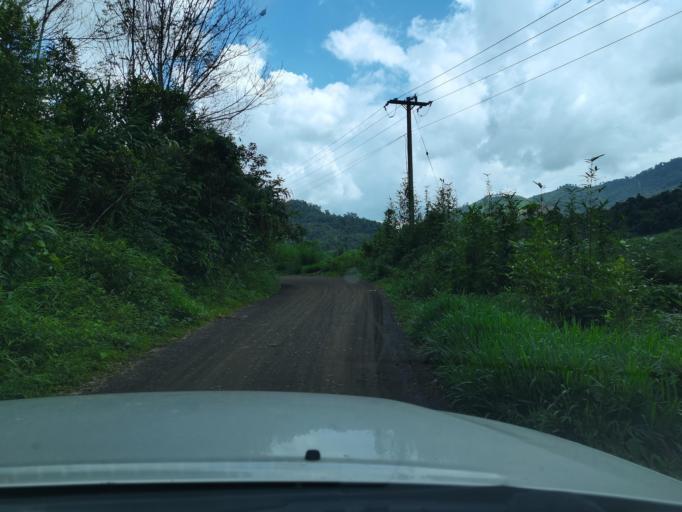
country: LA
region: Loungnamtha
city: Muang Long
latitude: 20.7515
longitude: 101.0183
